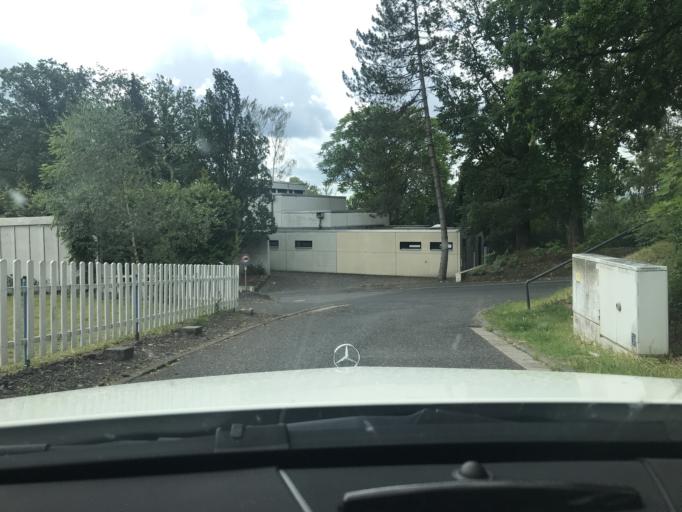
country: DE
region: Hesse
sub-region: Regierungsbezirk Kassel
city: Bad Hersfeld
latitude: 50.8726
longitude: 9.6979
